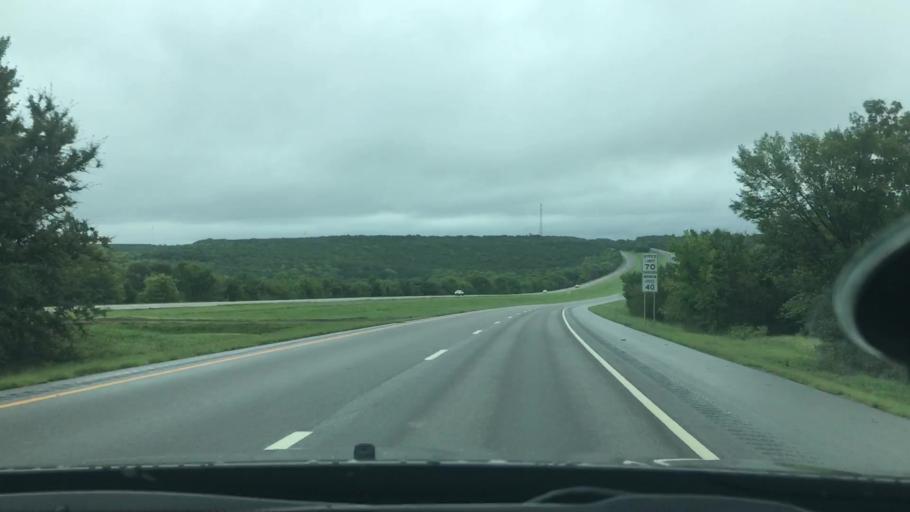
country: US
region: Oklahoma
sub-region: Okmulgee County
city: Henryetta
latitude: 35.4365
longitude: -95.8269
